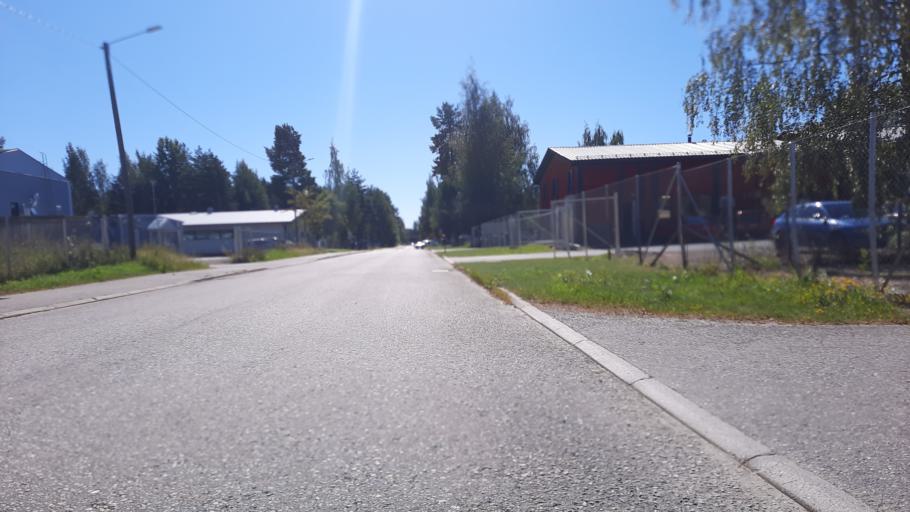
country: FI
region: North Karelia
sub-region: Joensuu
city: Joensuu
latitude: 62.6234
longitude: 29.7435
